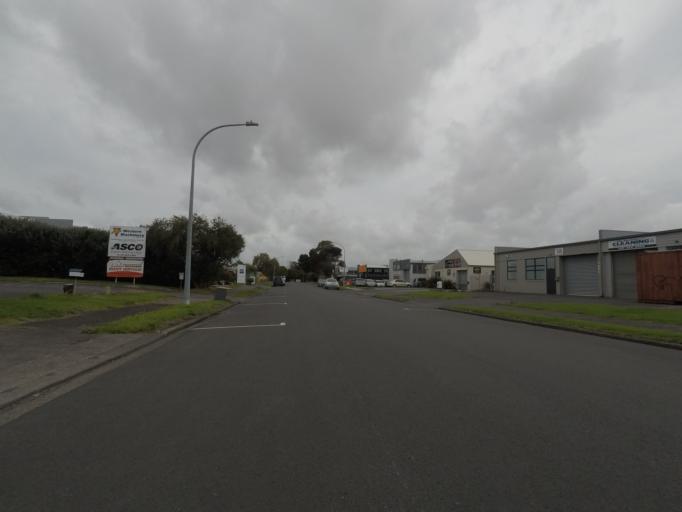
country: NZ
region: Auckland
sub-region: Auckland
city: Rosebank
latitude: -36.8826
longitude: 174.6774
